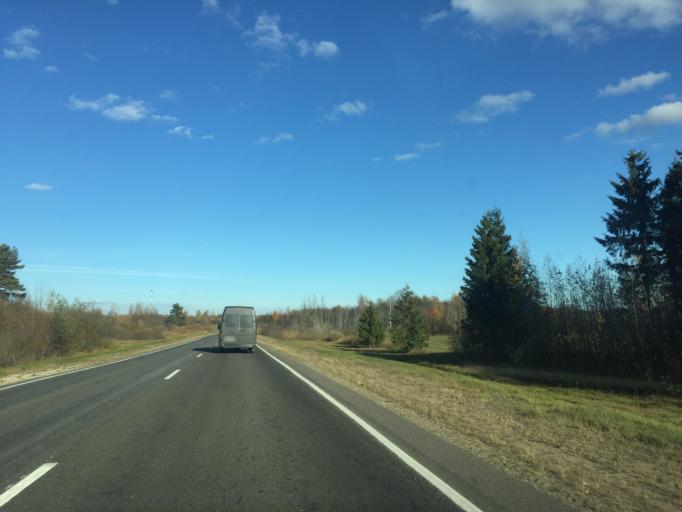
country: BY
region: Vitebsk
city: Dzisna
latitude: 55.2870
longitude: 28.1841
